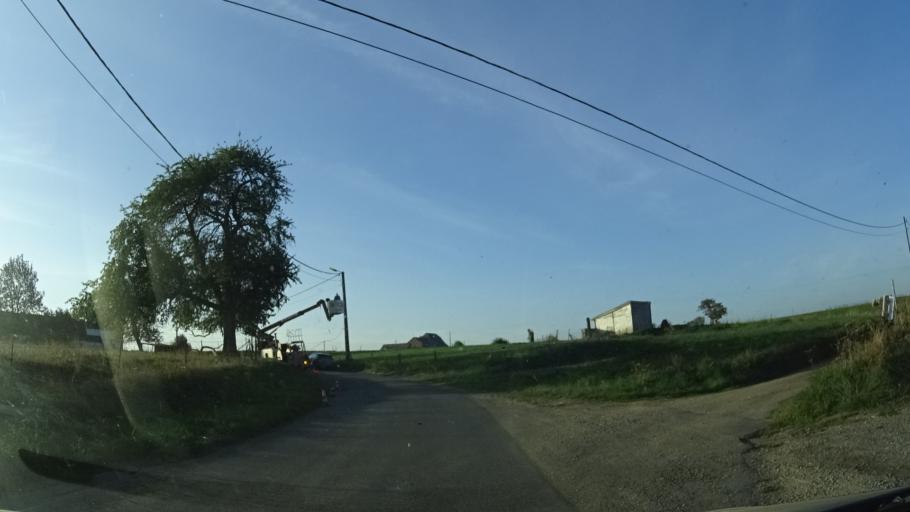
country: BE
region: Wallonia
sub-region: Province du Hainaut
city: Beaumont
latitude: 50.2486
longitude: 4.2612
